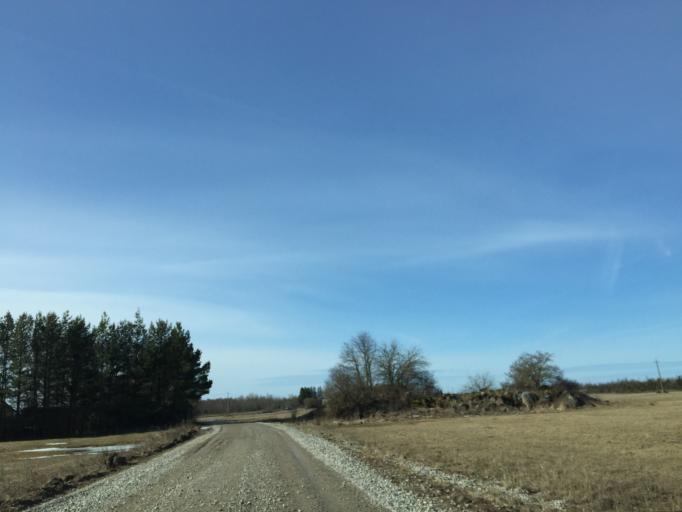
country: EE
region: Laeaene
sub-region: Haapsalu linn
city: Haapsalu
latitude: 58.6692
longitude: 23.5346
